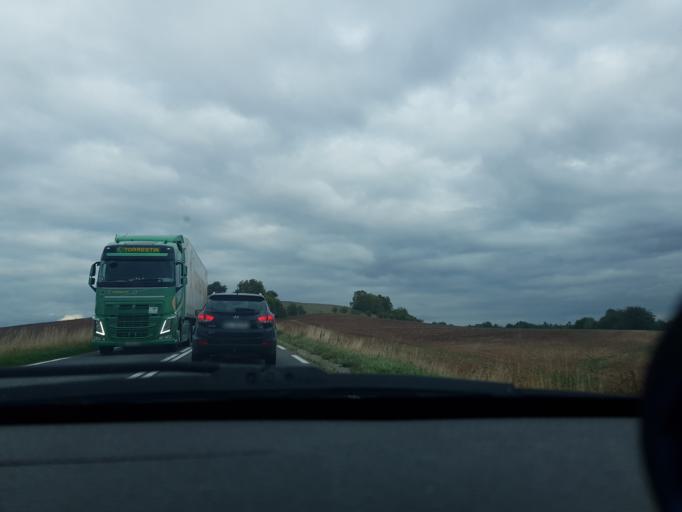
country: FR
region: Lorraine
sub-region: Departement de la Moselle
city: Morhange
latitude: 48.9080
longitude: 6.5620
